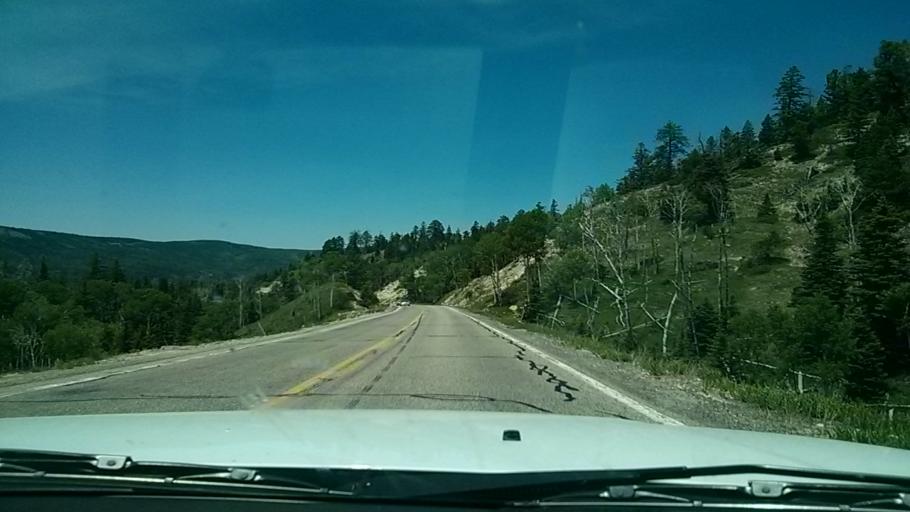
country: US
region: Utah
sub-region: Iron County
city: Cedar City
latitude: 37.5926
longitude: -112.8833
